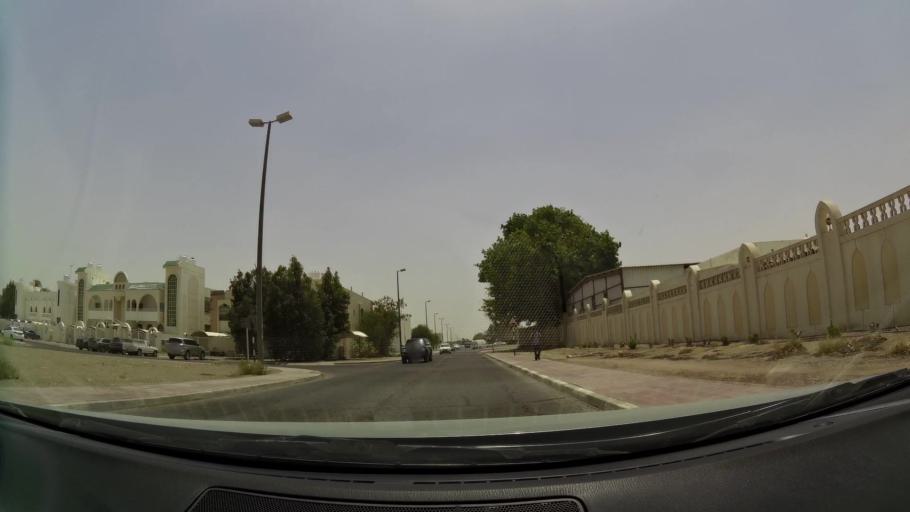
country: AE
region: Abu Dhabi
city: Al Ain
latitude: 24.2074
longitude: 55.7214
